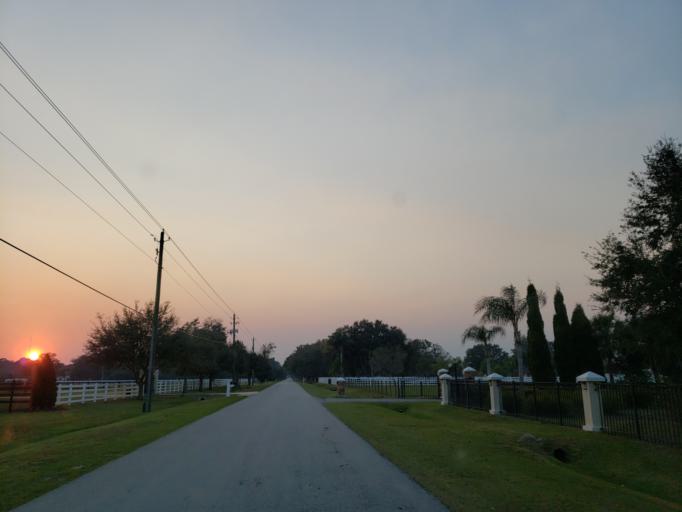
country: US
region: Florida
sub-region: Hillsborough County
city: Fish Hawk
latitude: 27.8427
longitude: -82.1807
